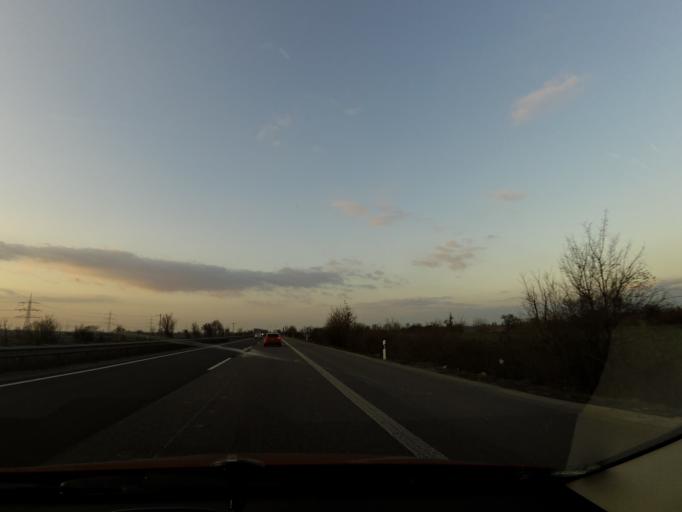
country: DE
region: Rheinland-Pfalz
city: Maxdorf
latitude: 49.4874
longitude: 8.3122
